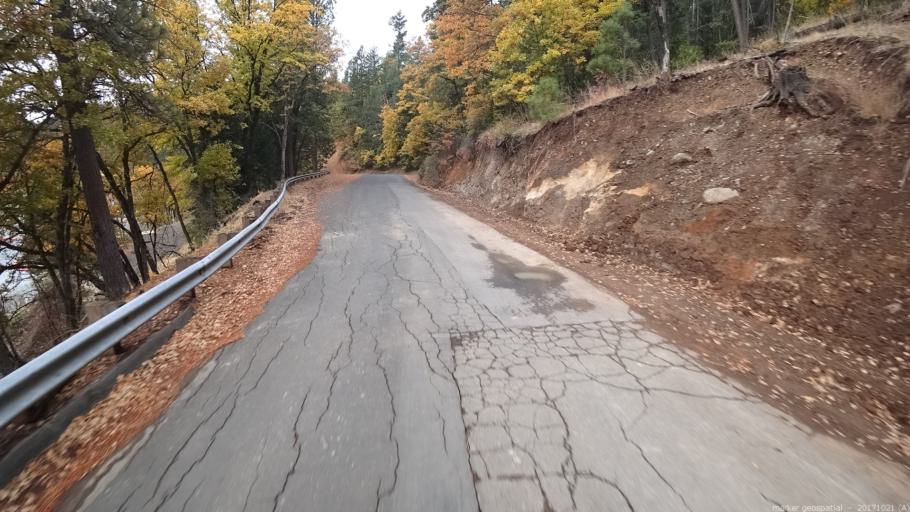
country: US
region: California
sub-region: Shasta County
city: Burney
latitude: 41.0238
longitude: -121.6758
